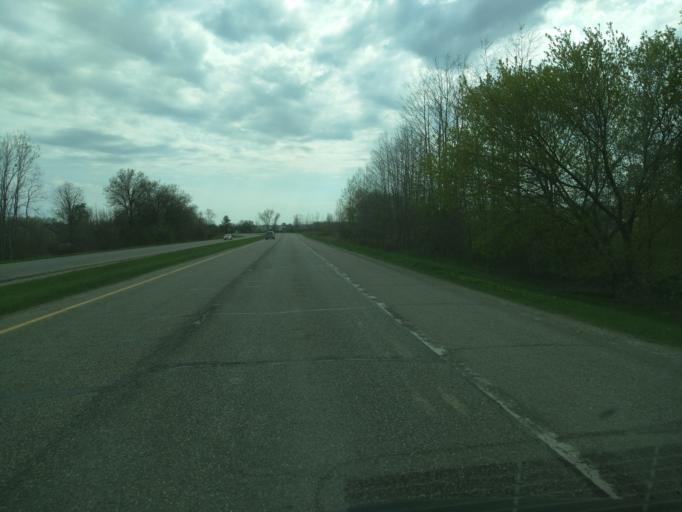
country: US
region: Michigan
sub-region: Eaton County
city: Waverly
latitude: 42.6966
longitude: -84.6306
